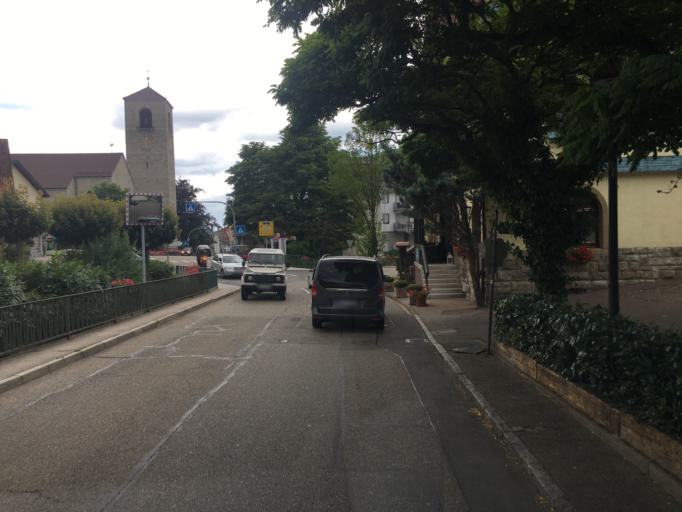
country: DE
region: Baden-Wuerttemberg
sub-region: Karlsruhe Region
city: Buhlertal
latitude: 48.7213
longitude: 8.1874
